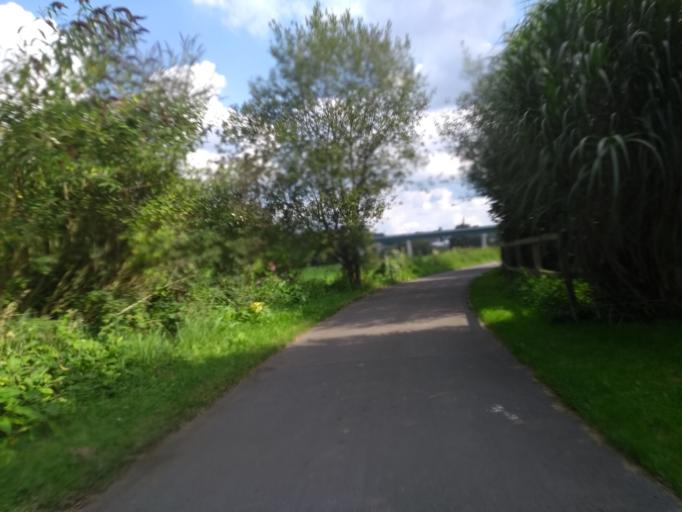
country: DE
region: North Rhine-Westphalia
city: Wetter (Ruhr)
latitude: 51.3903
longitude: 7.3741
